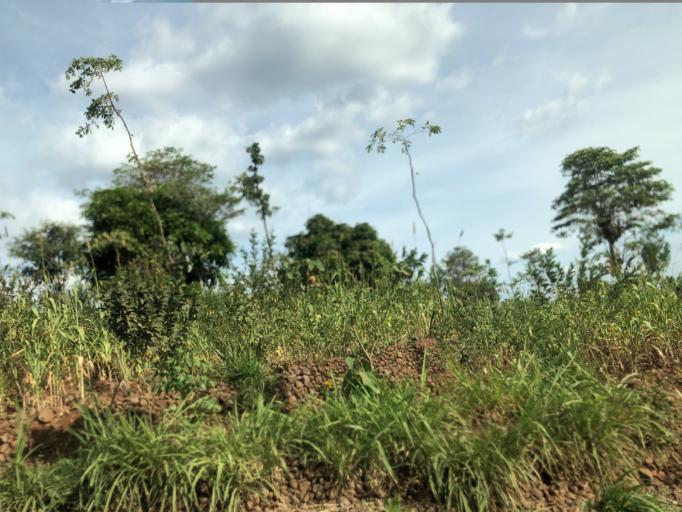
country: ET
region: Southern Nations, Nationalities, and People's Region
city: Konso
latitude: 5.2908
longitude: 37.3744
